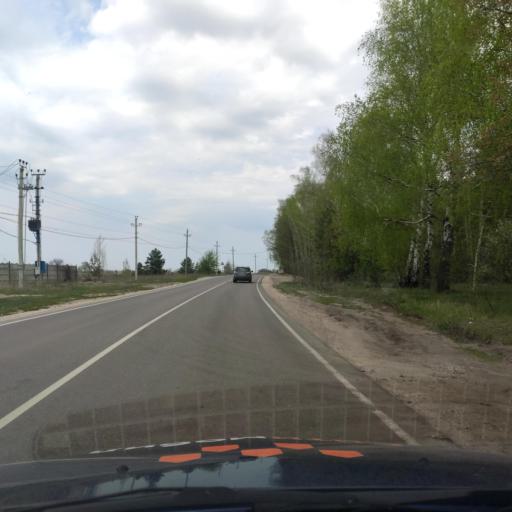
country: RU
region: Voronezj
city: Podgornoye
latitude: 51.8395
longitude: 39.1433
